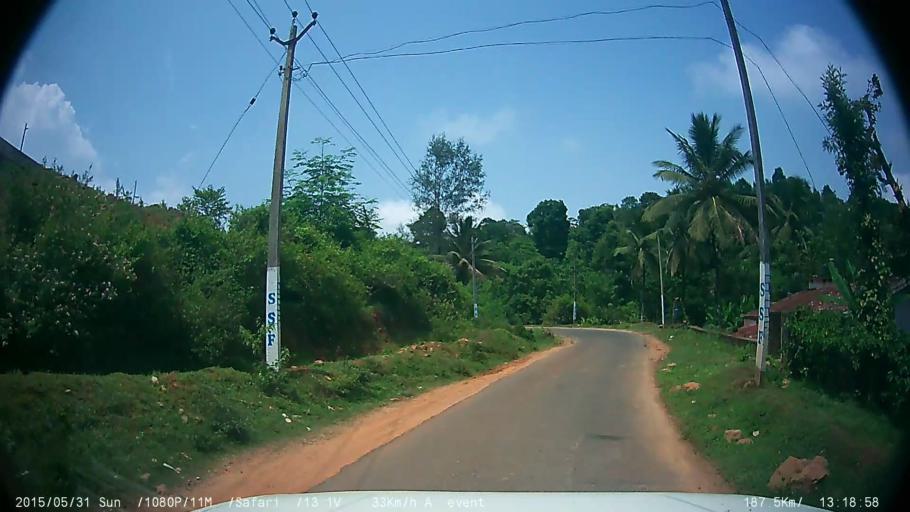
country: IN
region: Kerala
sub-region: Wayanad
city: Kalpetta
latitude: 11.5268
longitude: 76.1398
